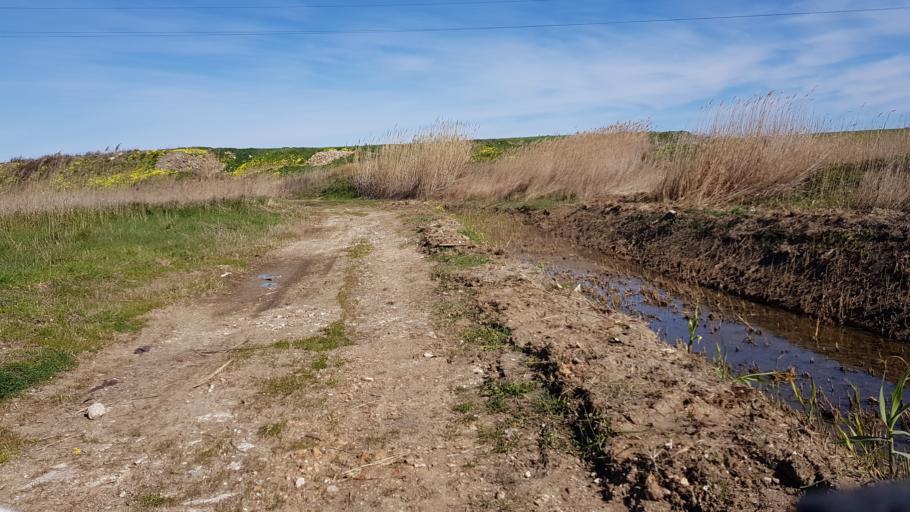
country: IT
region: Apulia
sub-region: Provincia di Brindisi
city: La Rosa
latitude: 40.6048
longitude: 17.9341
